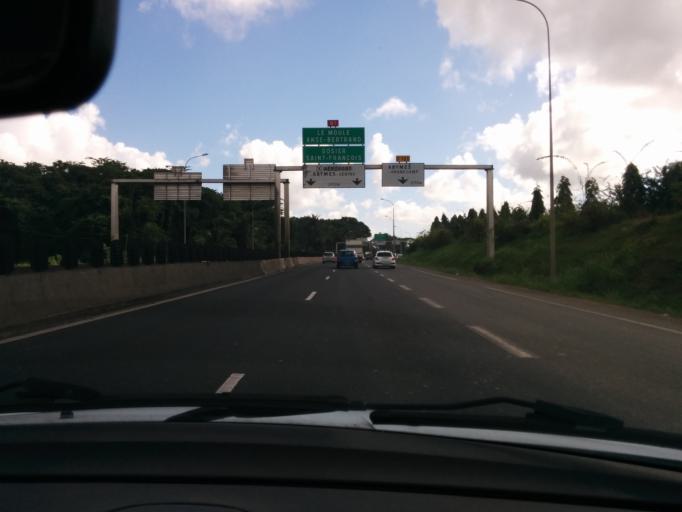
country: GP
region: Guadeloupe
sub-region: Guadeloupe
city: Pointe-a-Pitre
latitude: 16.2539
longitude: -61.5389
